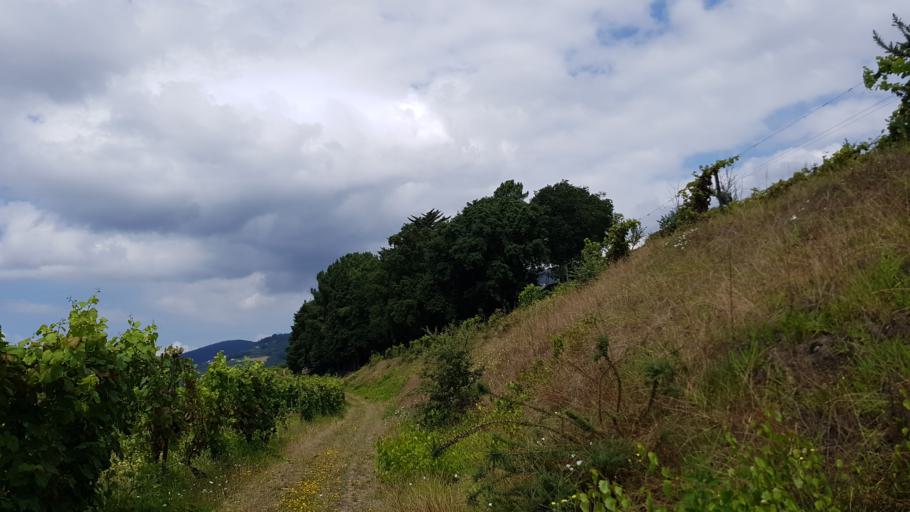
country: PT
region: Vila Real
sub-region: Mesao Frio
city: Mesao Frio
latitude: 41.1714
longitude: -7.8444
